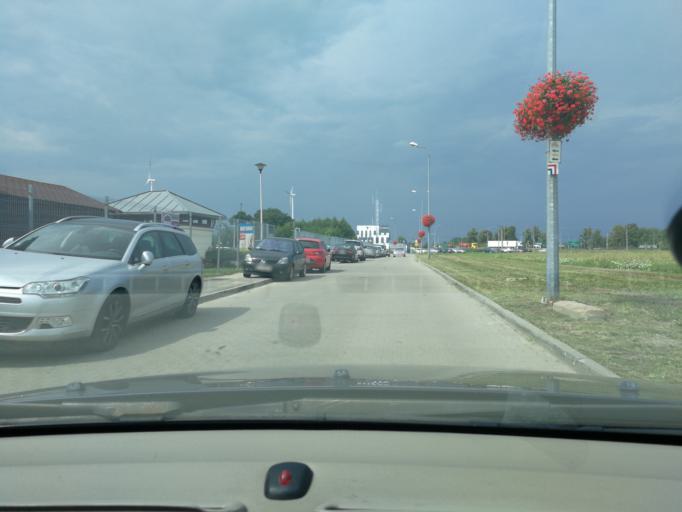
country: PL
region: Masovian Voivodeship
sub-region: Powiat zyrardowski
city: Mszczonow
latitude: 51.9783
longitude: 20.5267
